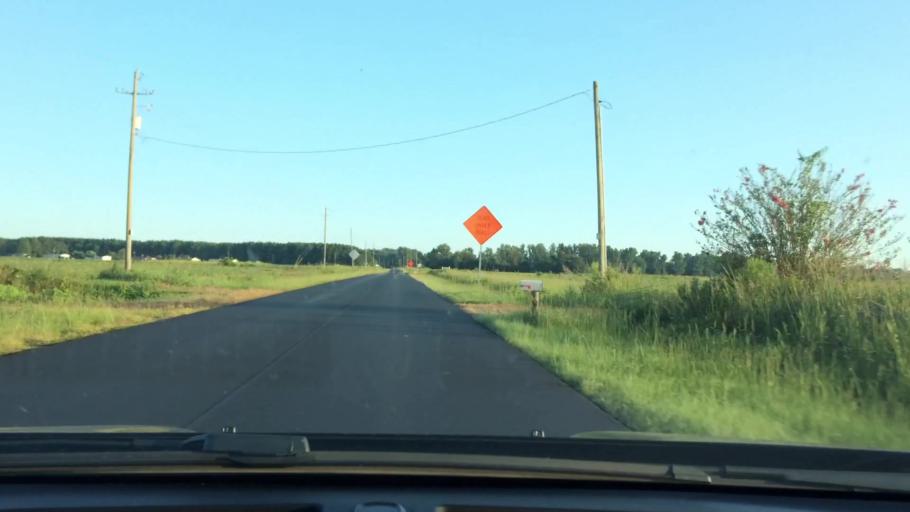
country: US
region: North Carolina
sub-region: Pitt County
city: Ayden
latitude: 35.4367
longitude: -77.4518
